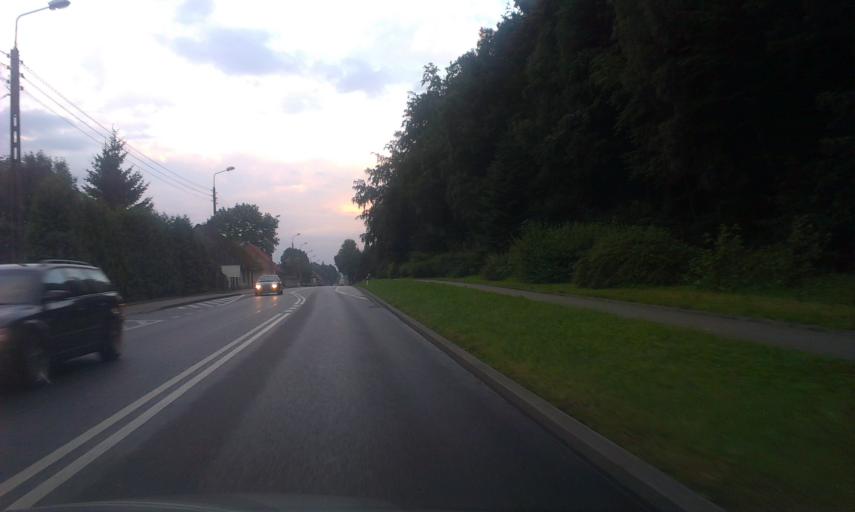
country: PL
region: West Pomeranian Voivodeship
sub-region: Powiat koszalinski
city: Sianow
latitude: 54.1279
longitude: 16.2967
